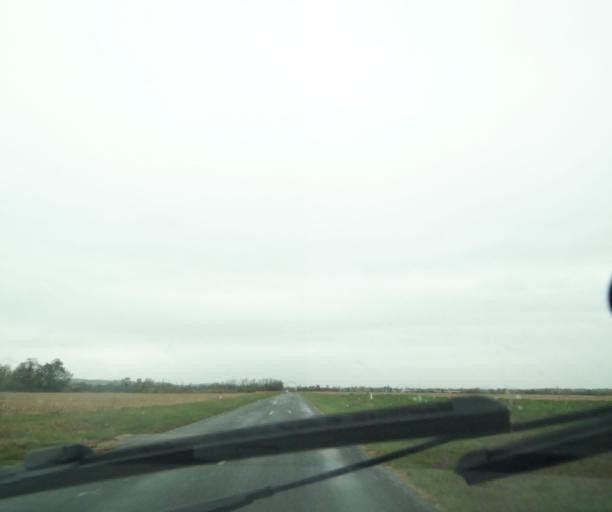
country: FR
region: Rhone-Alpes
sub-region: Departement de l'Ain
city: Loyettes
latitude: 45.7892
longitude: 5.2233
